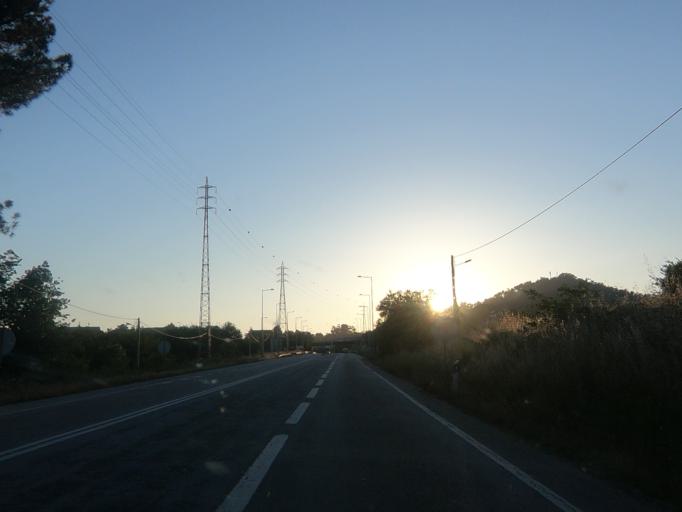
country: PT
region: Viseu
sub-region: Viseu
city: Abraveses
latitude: 40.6915
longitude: -7.9082
